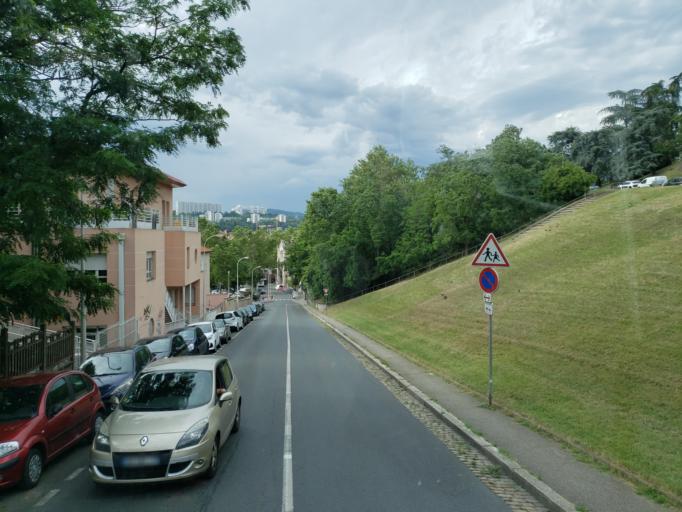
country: FR
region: Rhone-Alpes
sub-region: Departement du Rhone
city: Tassin-la-Demi-Lune
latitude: 45.7713
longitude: 4.8088
